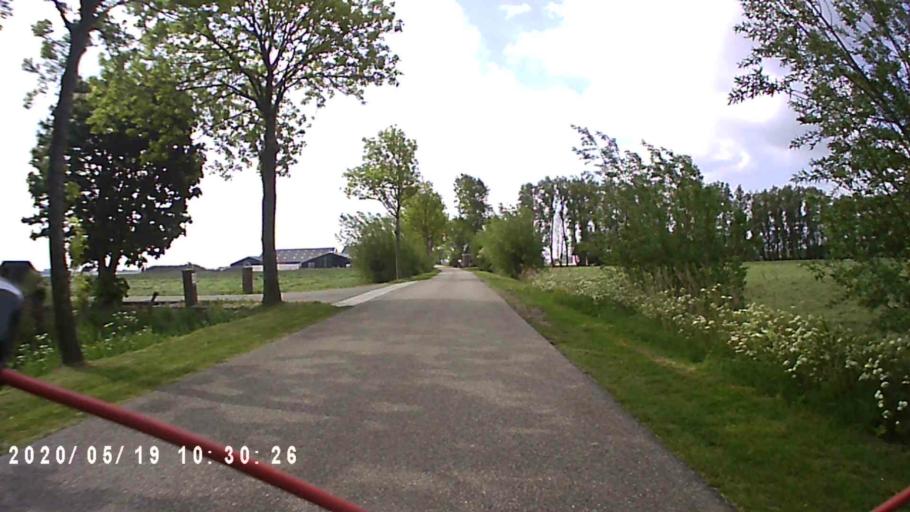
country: NL
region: Friesland
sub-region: Gemeente Kollumerland en Nieuwkruisland
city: Kollum
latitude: 53.2946
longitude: 6.1956
